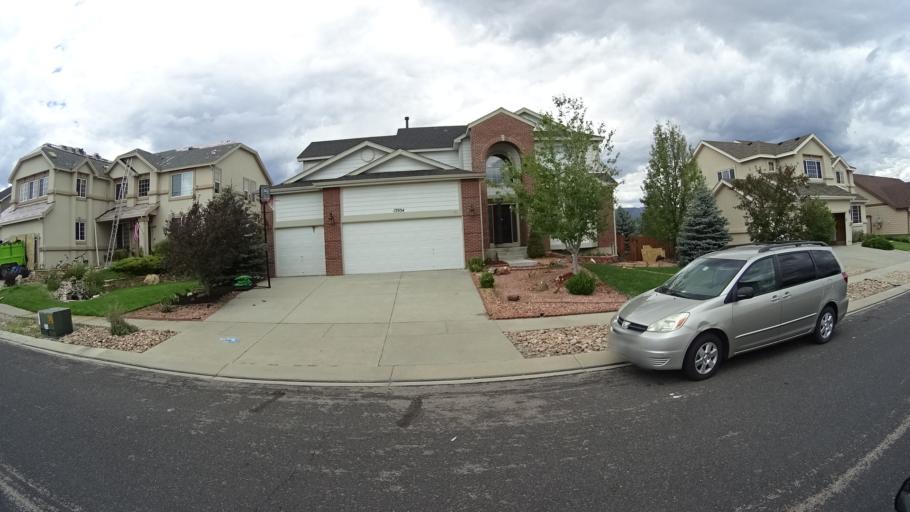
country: US
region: Colorado
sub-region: El Paso County
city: Gleneagle
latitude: 39.0331
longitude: -104.8127
